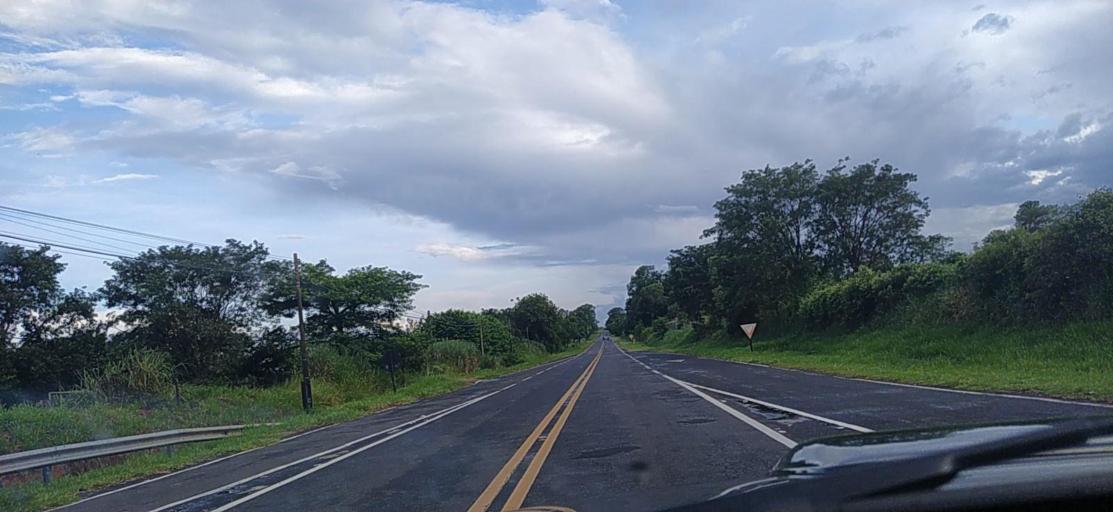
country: BR
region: Sao Paulo
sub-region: Catanduva
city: Catanduva
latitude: -21.1619
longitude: -48.9432
